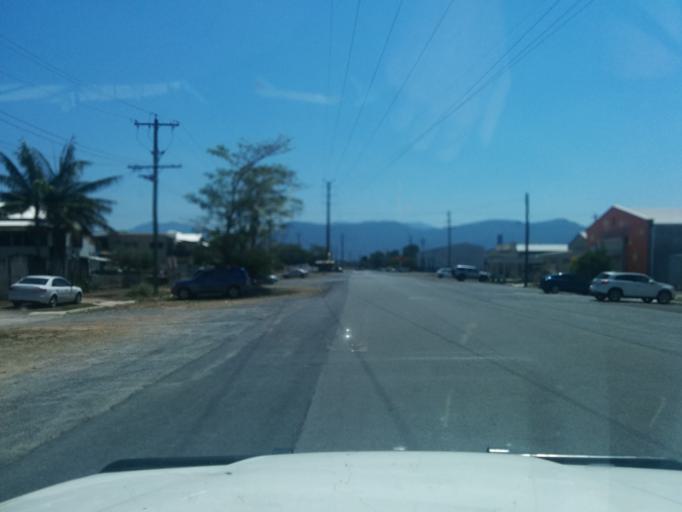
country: AU
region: Queensland
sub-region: Cairns
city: Cairns
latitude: -16.9289
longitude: 145.7750
